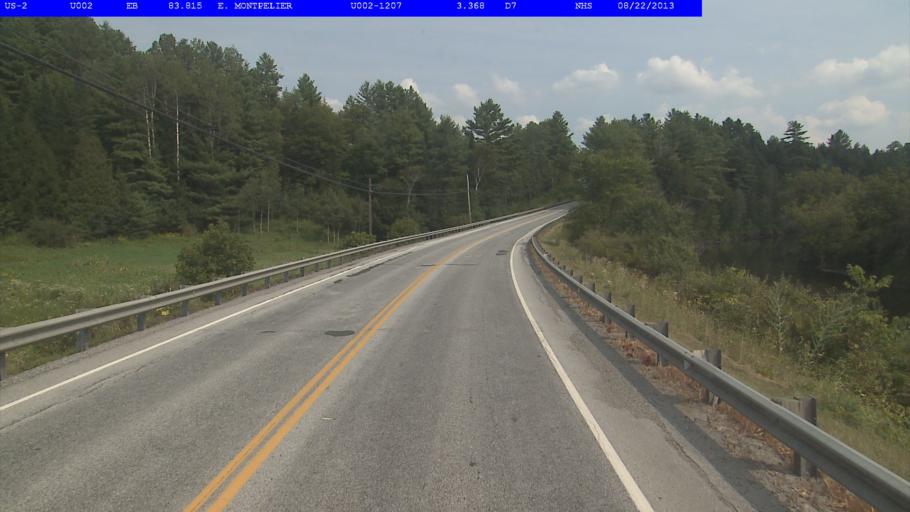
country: US
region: Vermont
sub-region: Washington County
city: Barre
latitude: 44.2717
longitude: -72.4783
